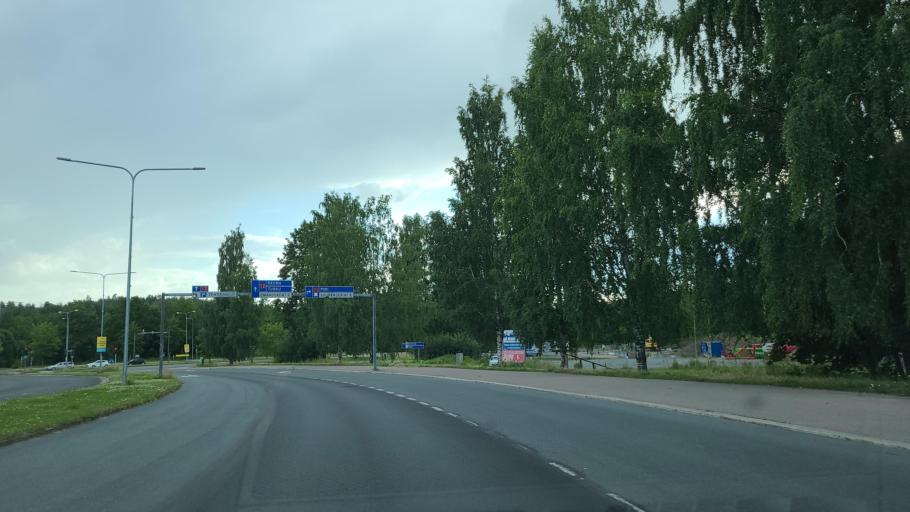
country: FI
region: Pirkanmaa
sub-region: Tampere
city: Nokia
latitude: 61.4759
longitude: 23.5066
